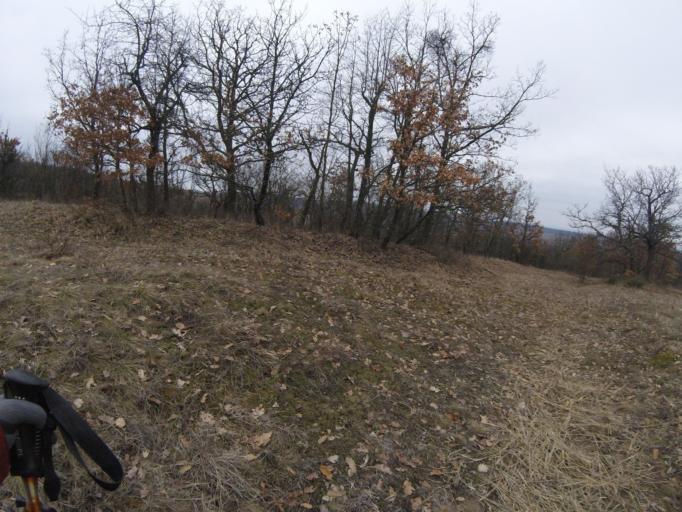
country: HU
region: Borsod-Abauj-Zemplen
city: Rudabanya
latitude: 48.4507
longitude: 20.6088
